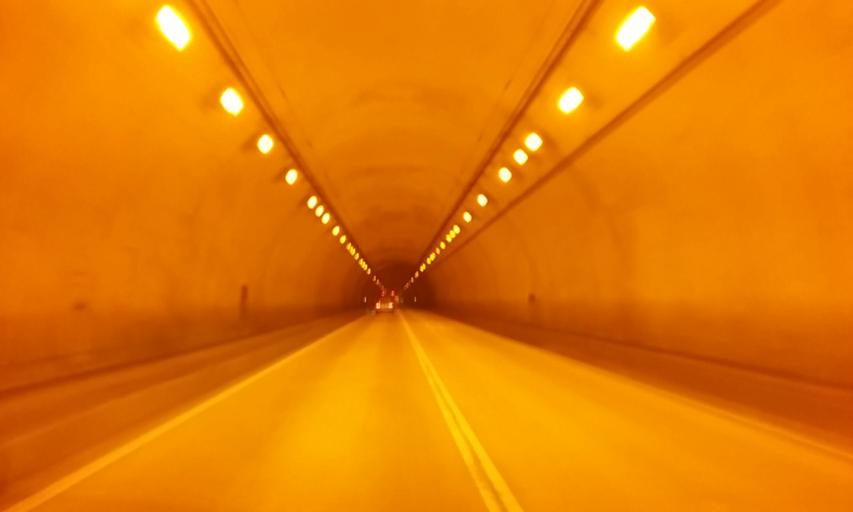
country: JP
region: Kyoto
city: Kameoka
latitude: 35.2294
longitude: 135.5743
